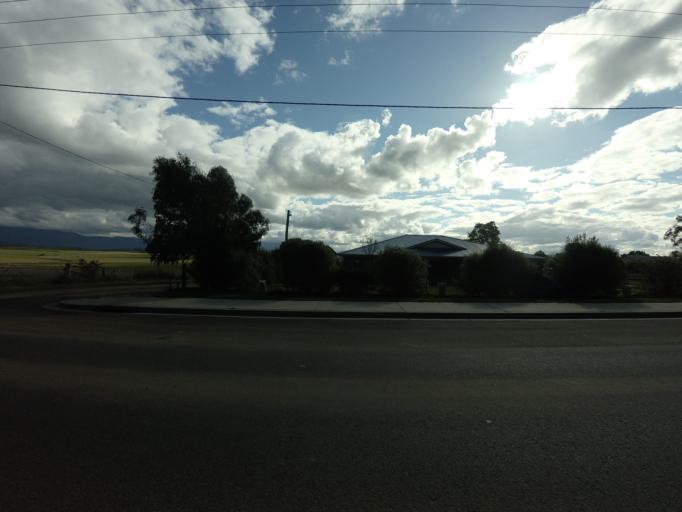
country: AU
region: Tasmania
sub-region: Northern Midlands
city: Longford
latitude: -41.6961
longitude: 147.0781
